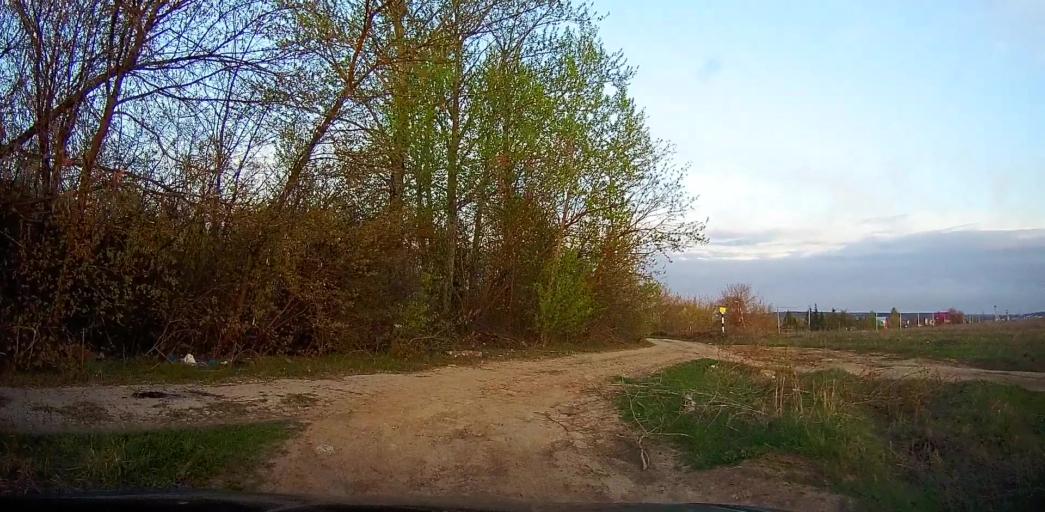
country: RU
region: Moskovskaya
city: Peski
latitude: 55.2318
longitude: 38.7316
